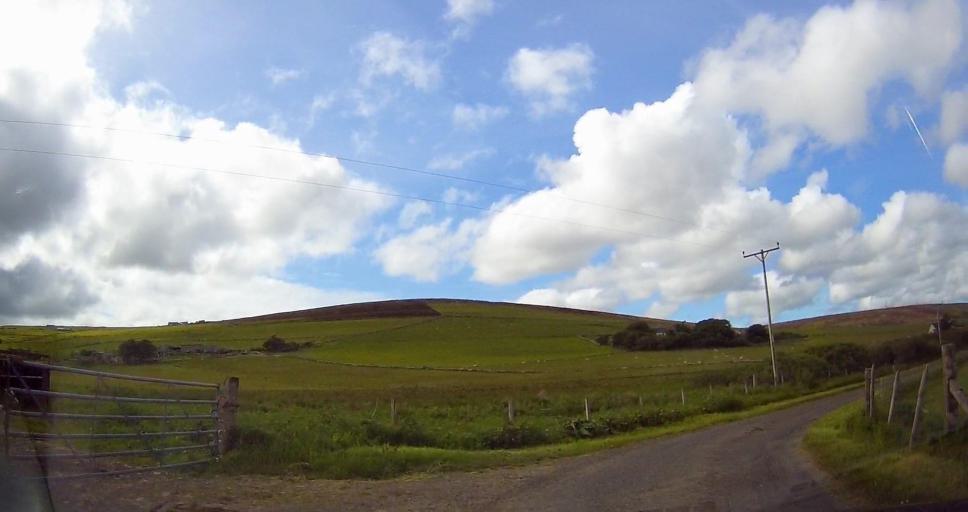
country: GB
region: Scotland
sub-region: Orkney Islands
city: Orkney
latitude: 59.0521
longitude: -3.1039
